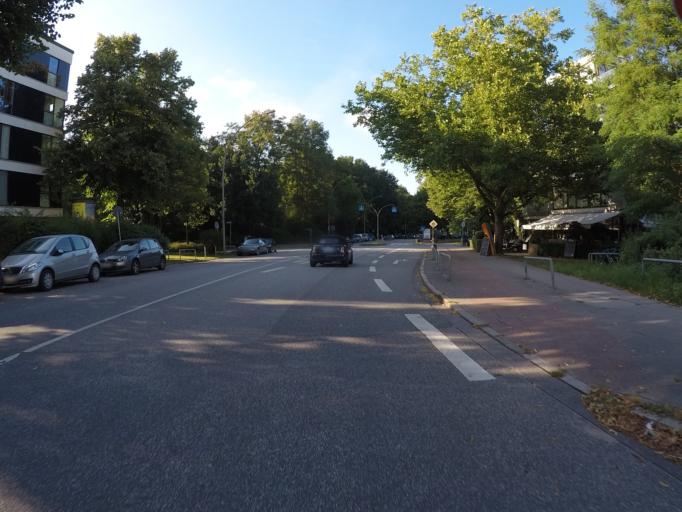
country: DE
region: Hamburg
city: Hamburg-Nord
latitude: 53.5850
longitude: 9.9883
